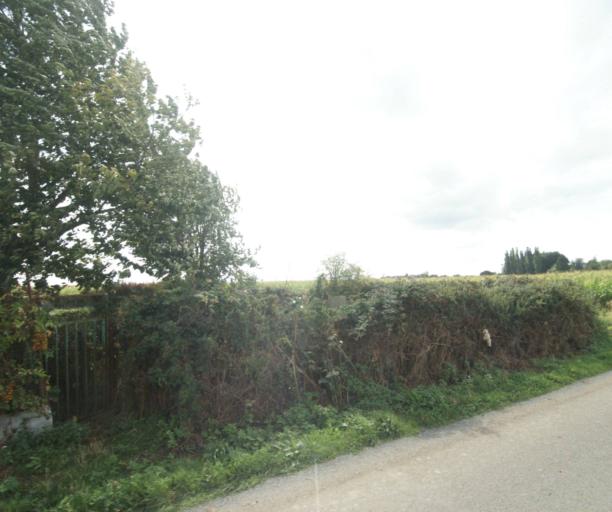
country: FR
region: Nord-Pas-de-Calais
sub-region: Departement du Nord
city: Faches-Thumesnil
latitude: 50.5919
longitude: 3.0657
